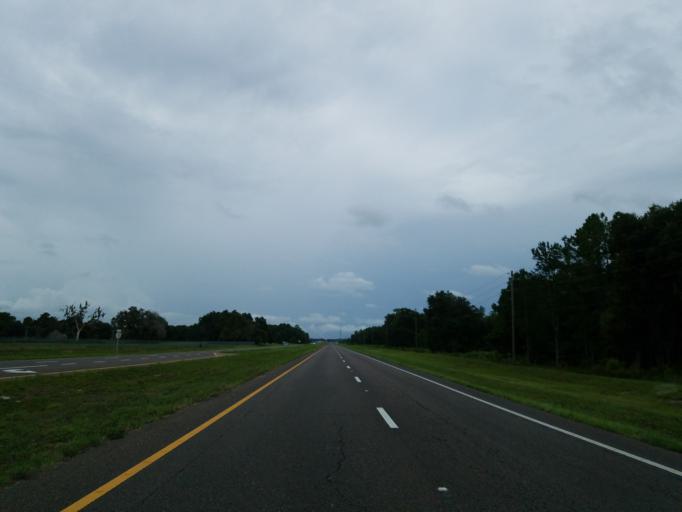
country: US
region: Florida
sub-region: Sumter County
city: Wildwood
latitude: 28.8792
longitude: -82.1186
